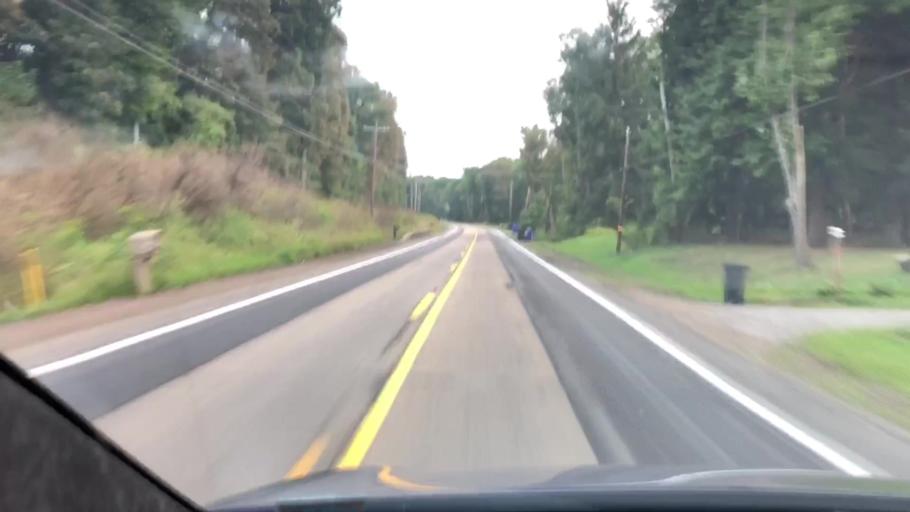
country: US
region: Pennsylvania
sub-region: Butler County
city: Slippery Rock
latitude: 41.0312
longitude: -80.0086
